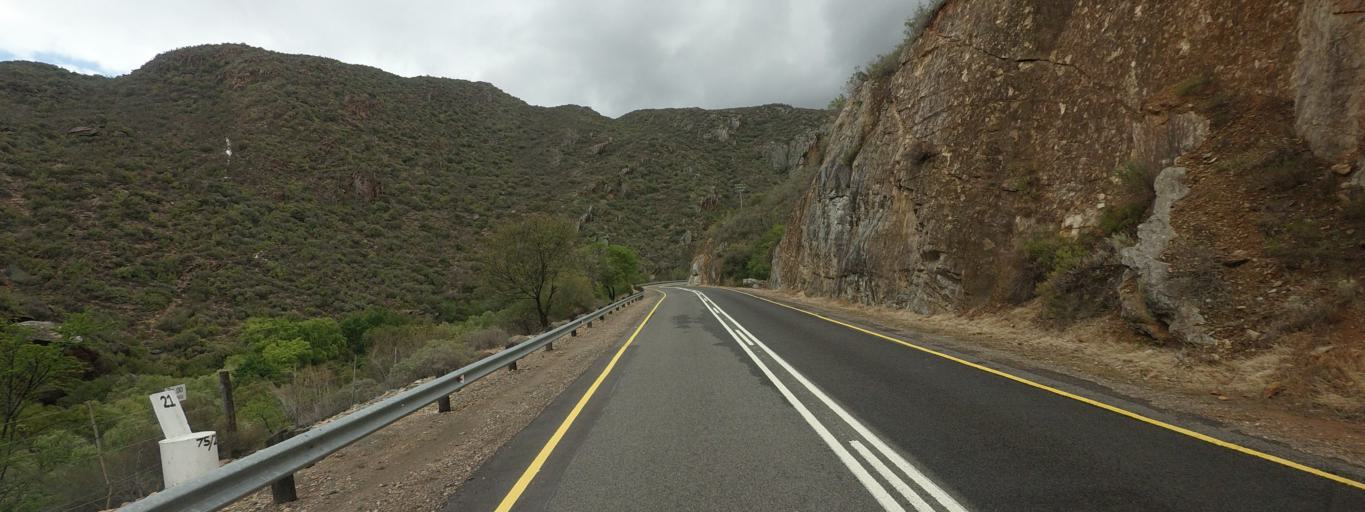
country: ZA
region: Western Cape
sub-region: Eden District Municipality
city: Oudtshoorn
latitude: -33.4339
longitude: 22.2538
